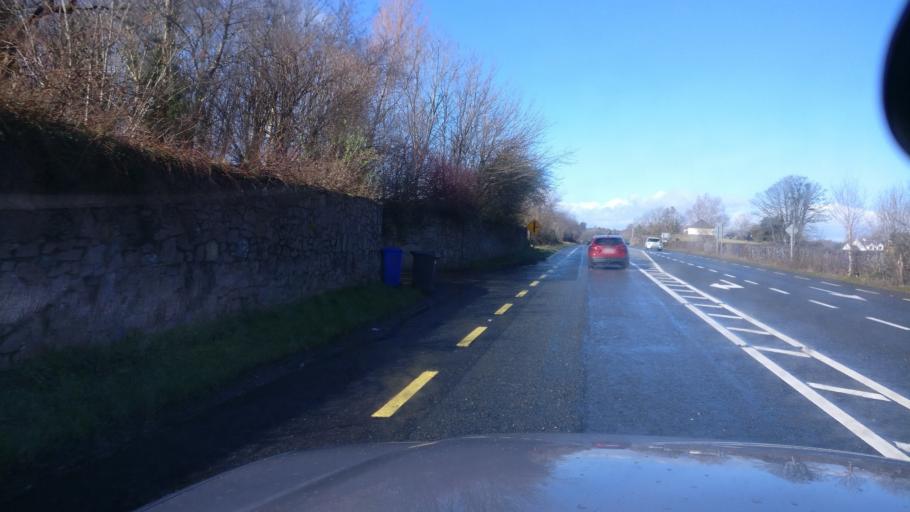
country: IE
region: Connaught
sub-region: County Galway
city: Moycullen
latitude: 53.3143
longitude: -9.1487
